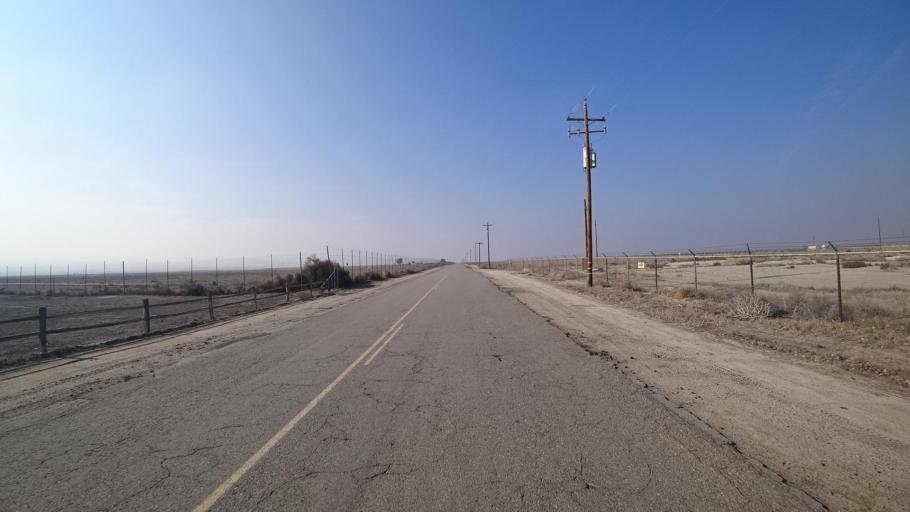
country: US
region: California
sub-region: Kern County
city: Buttonwillow
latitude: 35.3331
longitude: -119.3638
